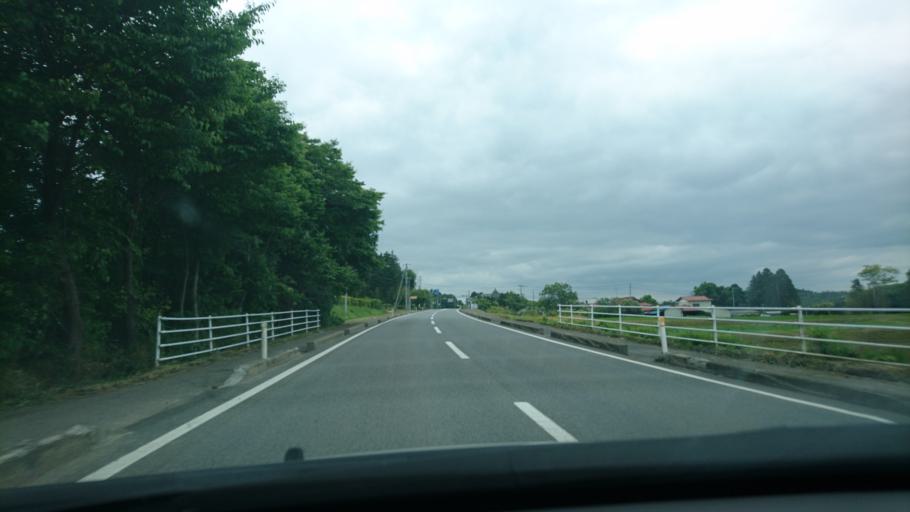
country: JP
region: Miyagi
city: Furukawa
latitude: 38.7175
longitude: 141.0344
